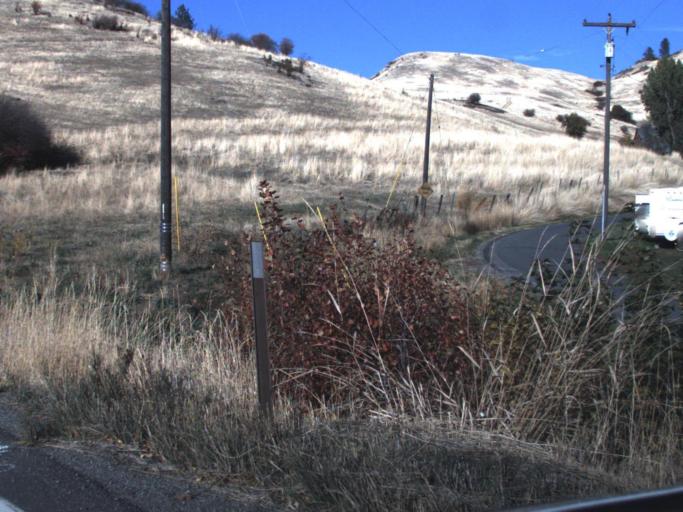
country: US
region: Washington
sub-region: Lincoln County
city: Davenport
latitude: 48.1198
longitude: -118.2051
